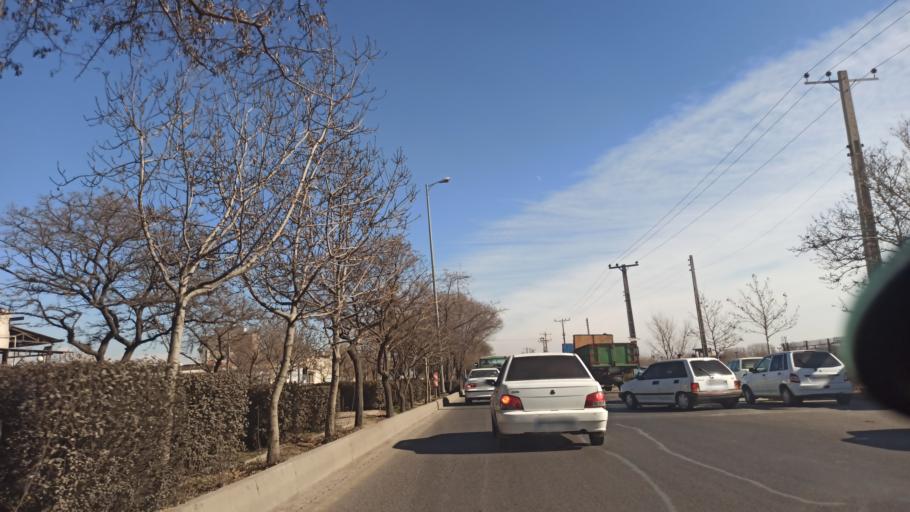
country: IR
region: Qazvin
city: Qazvin
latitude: 36.2580
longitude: 49.9880
